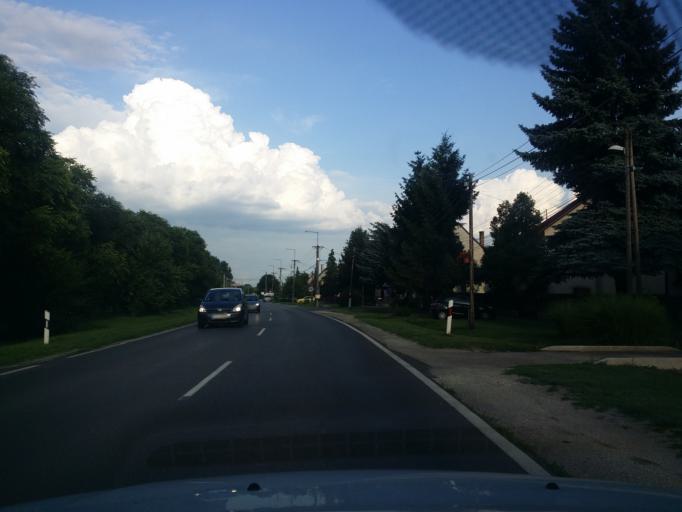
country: HU
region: Pest
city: Albertirsa
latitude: 47.2551
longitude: 19.5975
